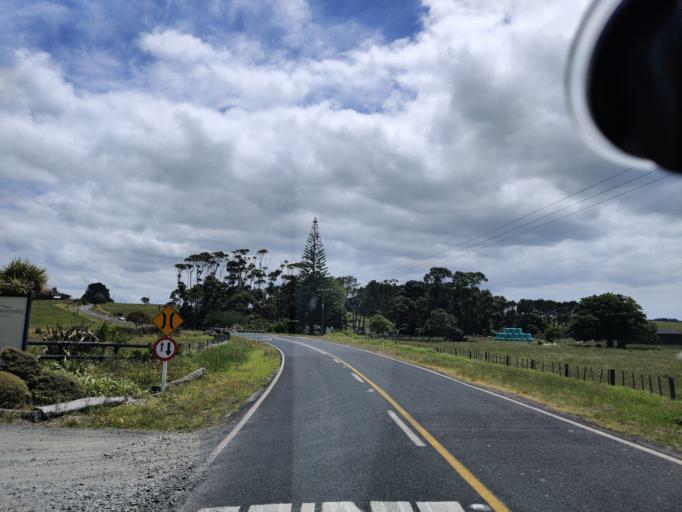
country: NZ
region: Northland
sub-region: Far North District
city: Kaitaia
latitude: -34.7091
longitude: 173.0347
